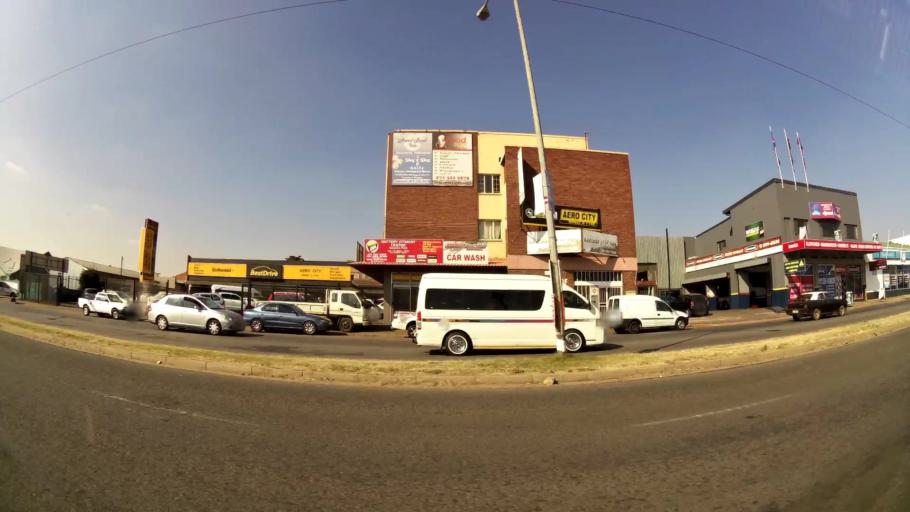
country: ZA
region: Gauteng
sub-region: City of Johannesburg Metropolitan Municipality
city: Modderfontein
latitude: -26.1135
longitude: 28.2289
